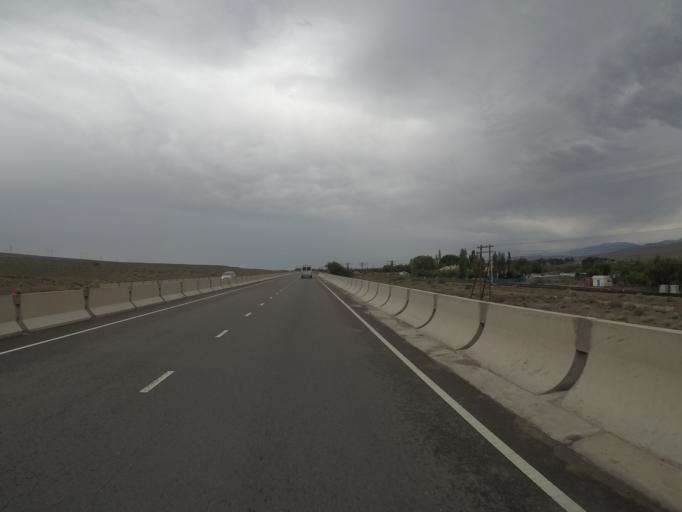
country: KG
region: Ysyk-Koel
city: Balykchy
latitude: 42.4666
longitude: 76.0349
